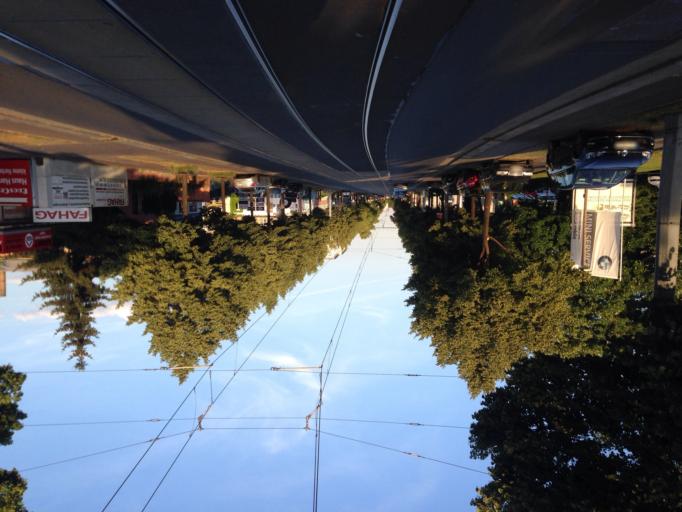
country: DE
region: Saxony
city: Dresden
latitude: 51.0595
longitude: 13.6992
